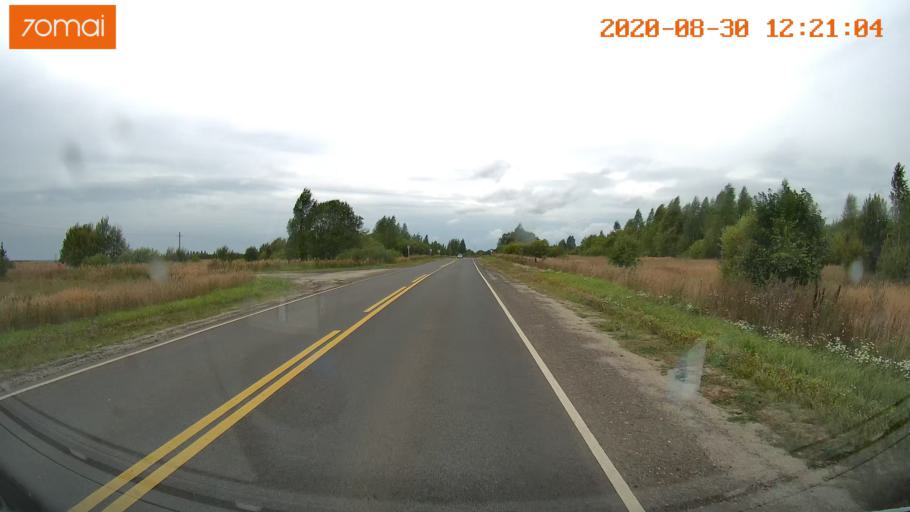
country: RU
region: Ivanovo
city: Yur'yevets
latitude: 57.3239
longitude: 42.8843
